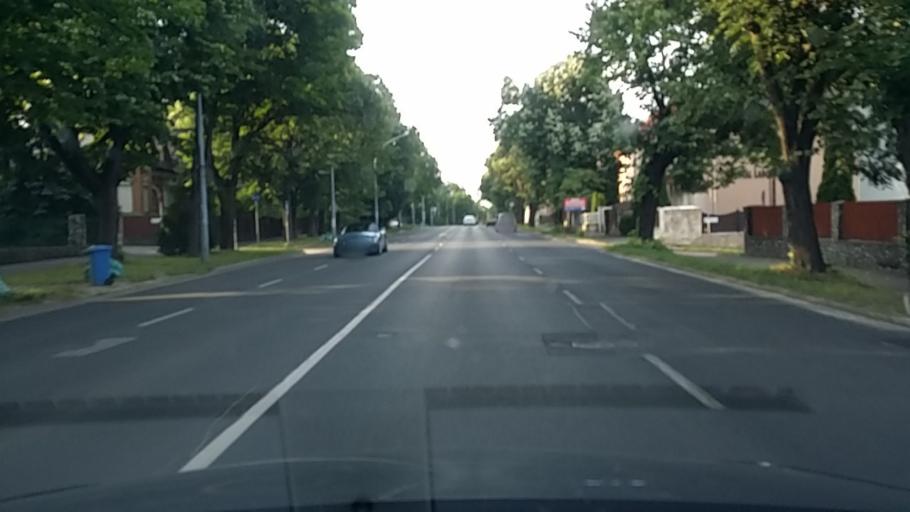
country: HU
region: Borsod-Abauj-Zemplen
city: Miskolc
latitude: 48.0869
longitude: 20.7856
